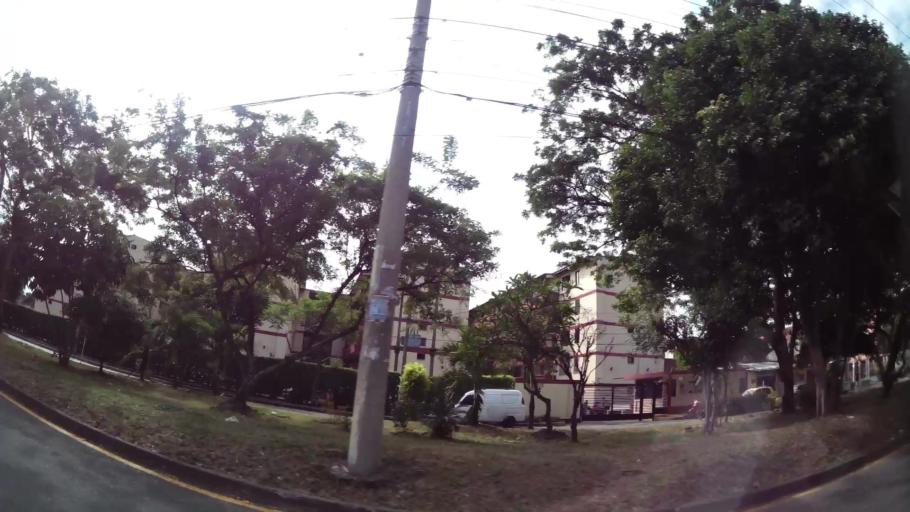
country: CO
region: Valle del Cauca
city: Cali
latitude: 3.4817
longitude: -76.4920
